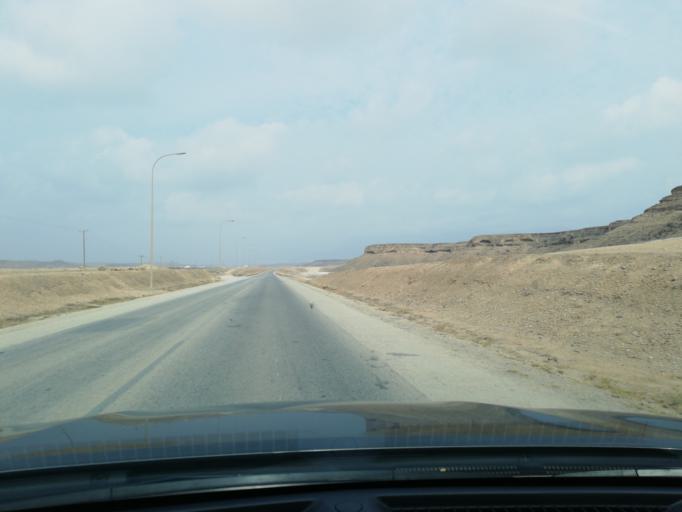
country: OM
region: Zufar
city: Salalah
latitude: 16.9530
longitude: 53.9234
